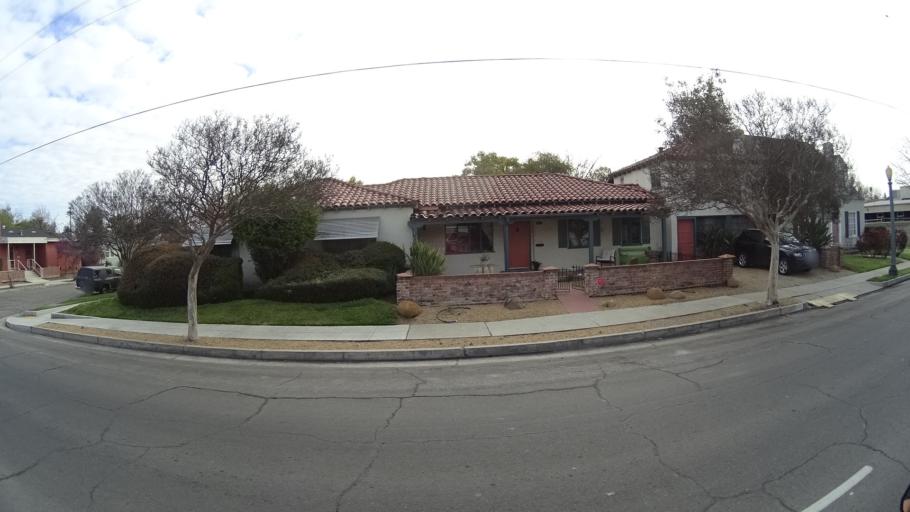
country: US
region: California
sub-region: Fresno County
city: Fresno
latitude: 36.7641
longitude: -119.8011
